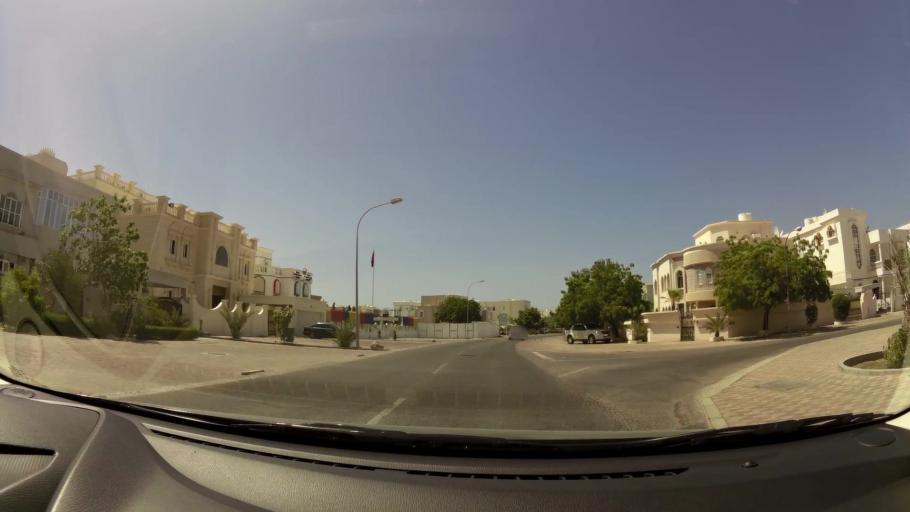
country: OM
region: Muhafazat Masqat
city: Bawshar
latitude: 23.5989
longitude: 58.3649
